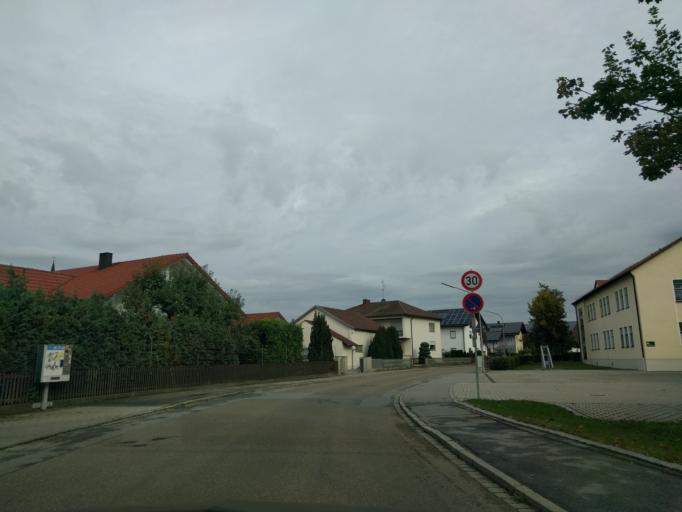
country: DE
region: Bavaria
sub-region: Lower Bavaria
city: Wallersdorf
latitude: 48.7363
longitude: 12.7512
